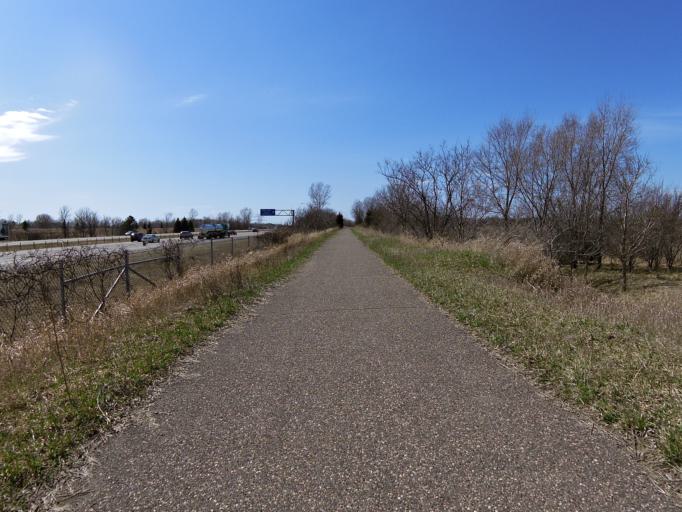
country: US
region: Minnesota
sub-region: Washington County
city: Lakeland
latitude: 44.9519
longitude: -92.8080
